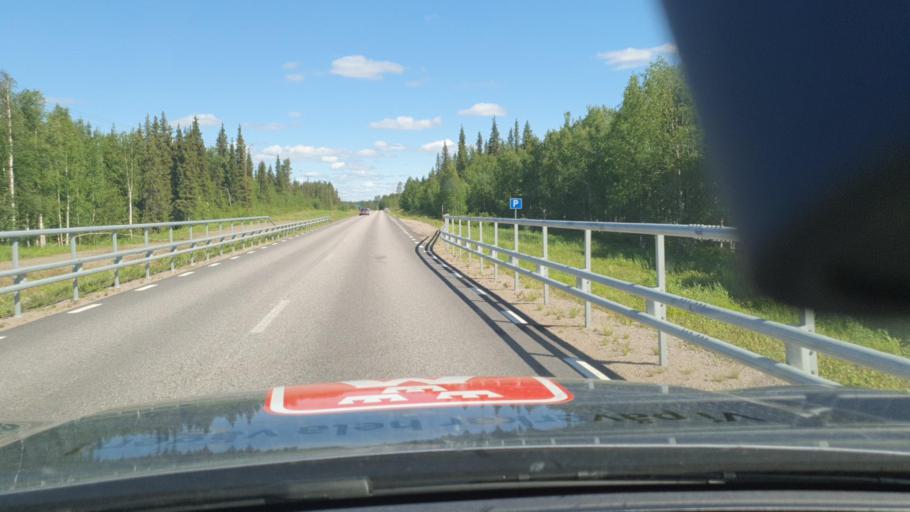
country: SE
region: Norrbotten
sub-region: Overkalix Kommun
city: OEverkalix
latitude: 67.0537
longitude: 22.5070
